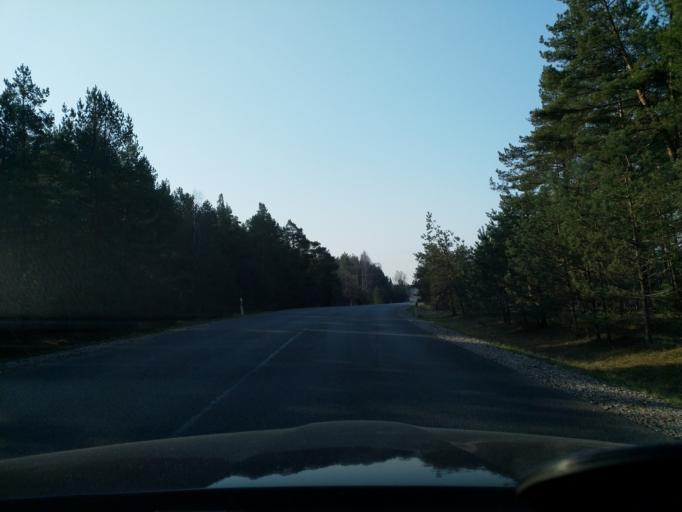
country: LT
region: Klaipedos apskritis
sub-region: Palanga
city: Sventoji
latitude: 56.0418
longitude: 21.1194
